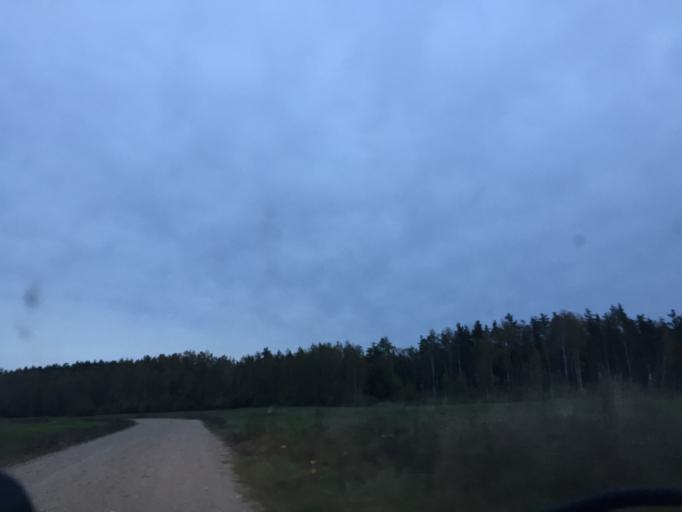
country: LV
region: Garkalne
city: Garkalne
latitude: 57.0824
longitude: 24.3805
